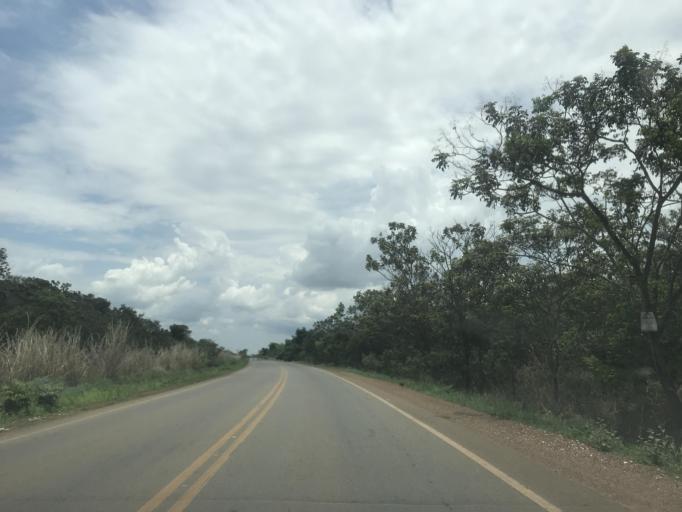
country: BR
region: Goias
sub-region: Vianopolis
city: Vianopolis
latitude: -16.7337
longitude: -48.4455
